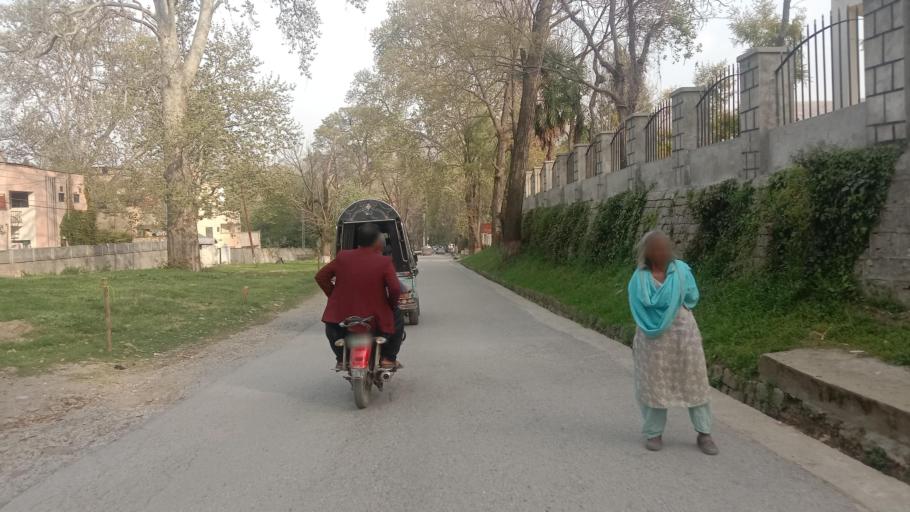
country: PK
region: Khyber Pakhtunkhwa
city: Abbottabad
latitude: 34.1518
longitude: 73.2135
